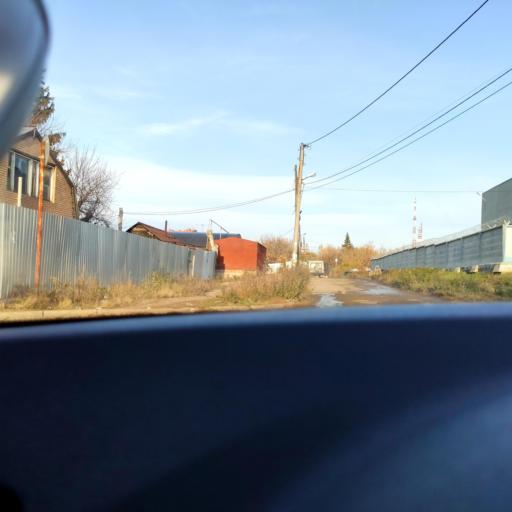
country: RU
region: Samara
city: Samara
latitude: 53.2238
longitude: 50.1772
